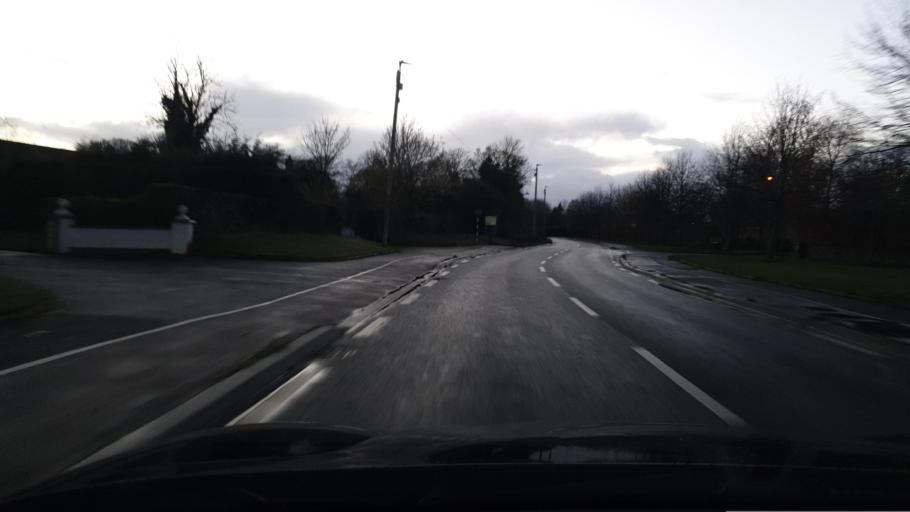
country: IE
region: Leinster
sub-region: Kildare
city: Maynooth
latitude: 53.3746
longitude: -6.6055
